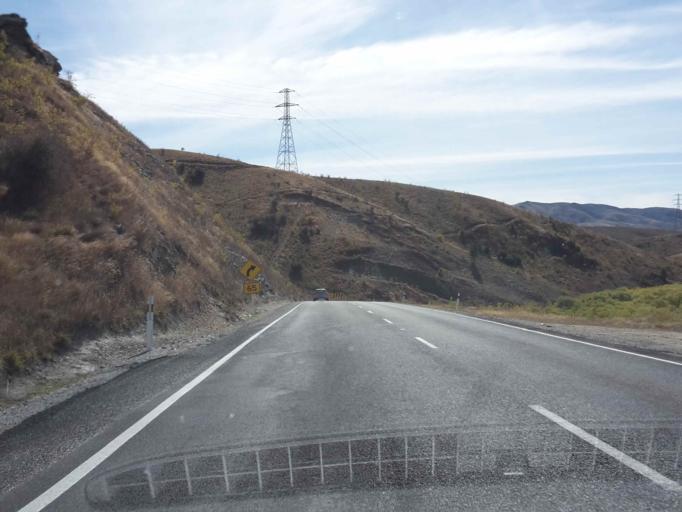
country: NZ
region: Otago
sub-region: Queenstown-Lakes District
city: Wanaka
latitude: -44.8002
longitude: 169.5064
